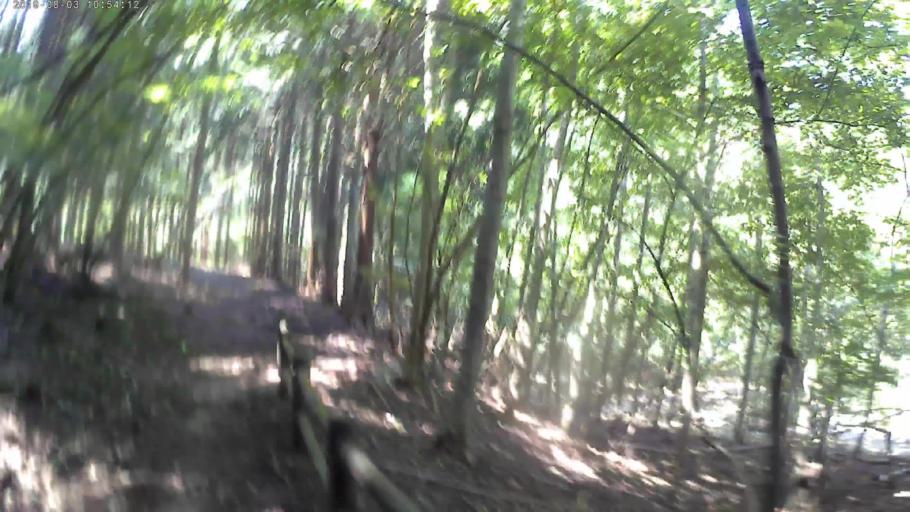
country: JP
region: Yamanashi
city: Enzan
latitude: 35.6204
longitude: 138.7719
